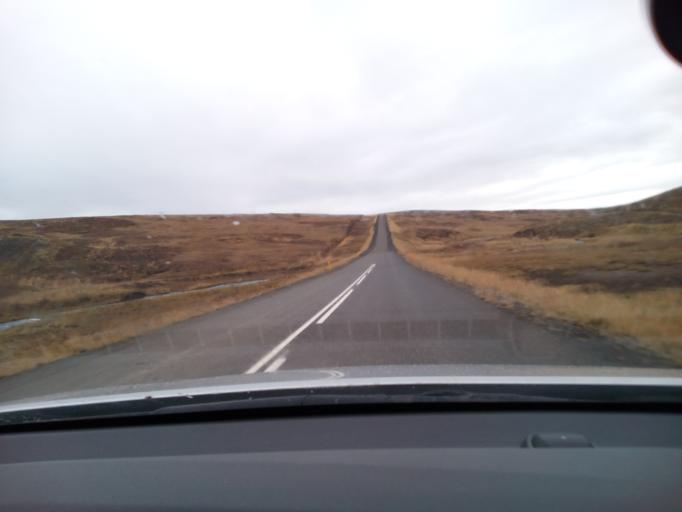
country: IS
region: Northeast
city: Laugar
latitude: 65.7928
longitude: -17.2349
